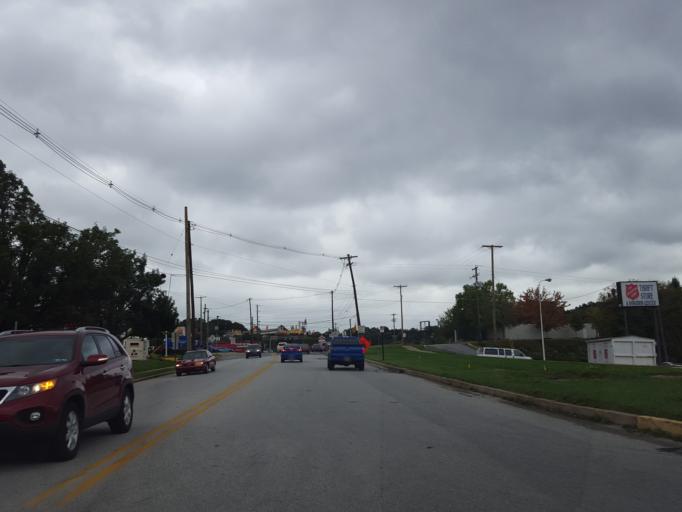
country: US
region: Pennsylvania
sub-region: York County
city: East York
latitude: 39.9598
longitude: -76.6818
